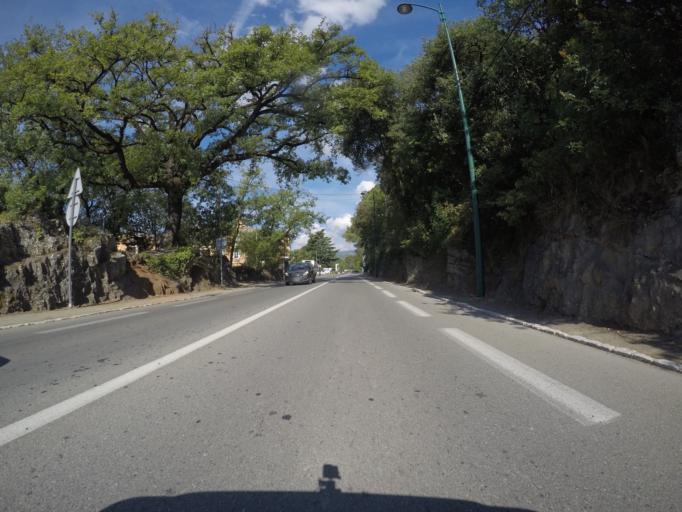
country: FR
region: Provence-Alpes-Cote d'Azur
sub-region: Departement des Alpes-Maritimes
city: Le Rouret
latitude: 43.6668
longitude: 7.0488
